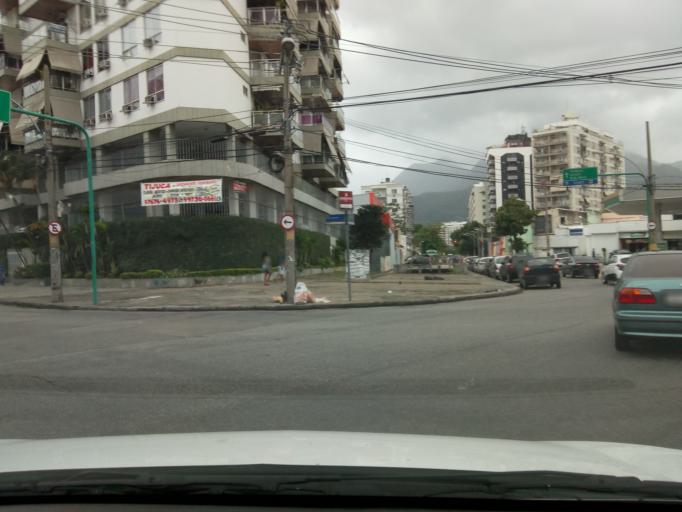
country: BR
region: Rio de Janeiro
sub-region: Rio De Janeiro
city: Rio de Janeiro
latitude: -22.9168
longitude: -43.2401
